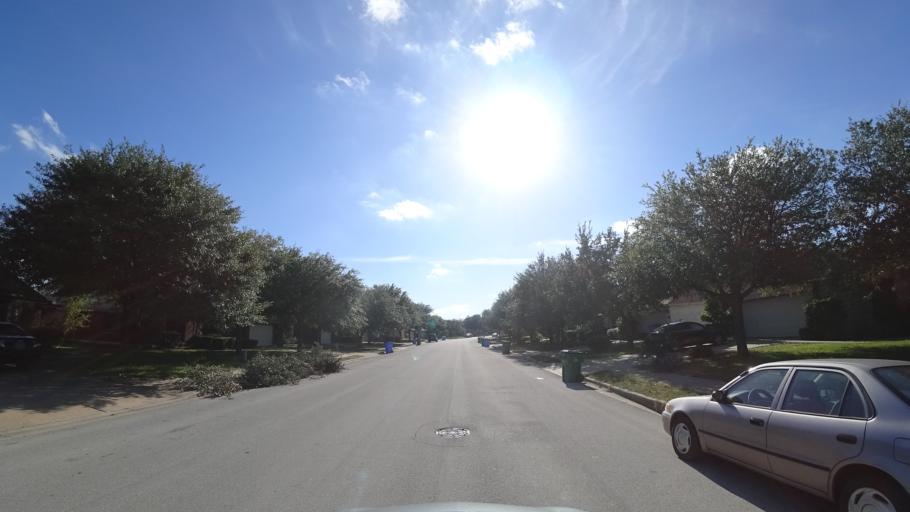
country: US
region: Texas
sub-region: Travis County
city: Wells Branch
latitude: 30.4642
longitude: -97.6847
